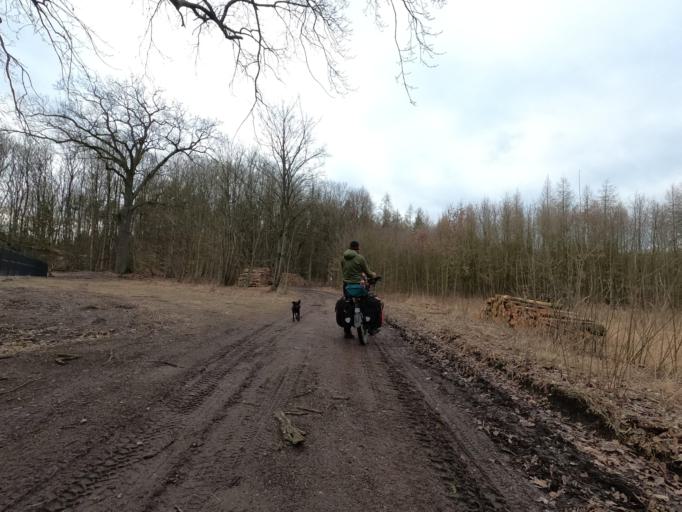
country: PL
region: Greater Poland Voivodeship
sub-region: Powiat pilski
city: Bialosliwie
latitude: 53.0975
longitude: 17.0943
